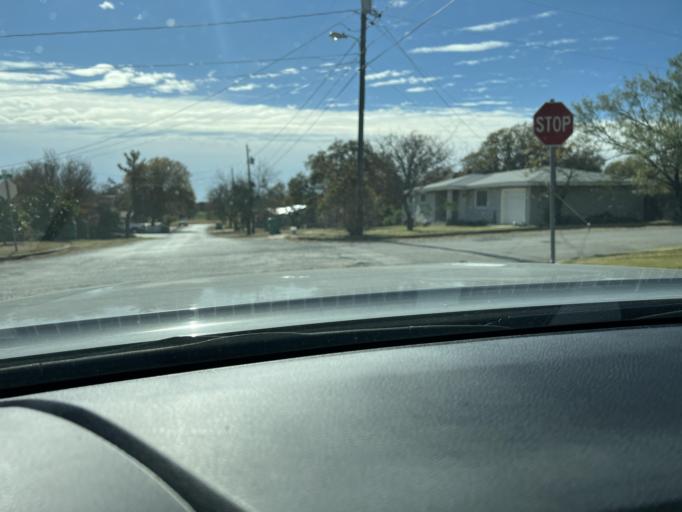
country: US
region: Texas
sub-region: Eastland County
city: Eastland
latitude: 32.3969
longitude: -98.8191
